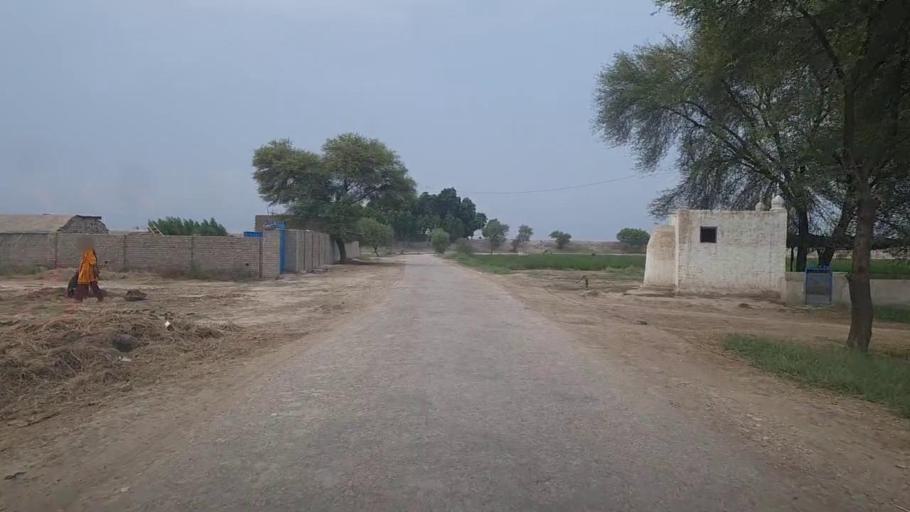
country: PK
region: Sindh
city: Kashmor
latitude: 28.3767
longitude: 69.7836
